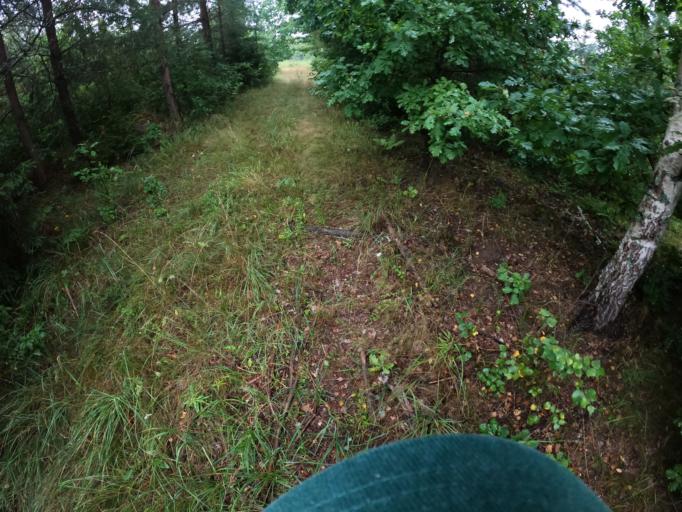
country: LV
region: Skrunda
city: Skrunda
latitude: 56.7975
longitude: 21.8423
